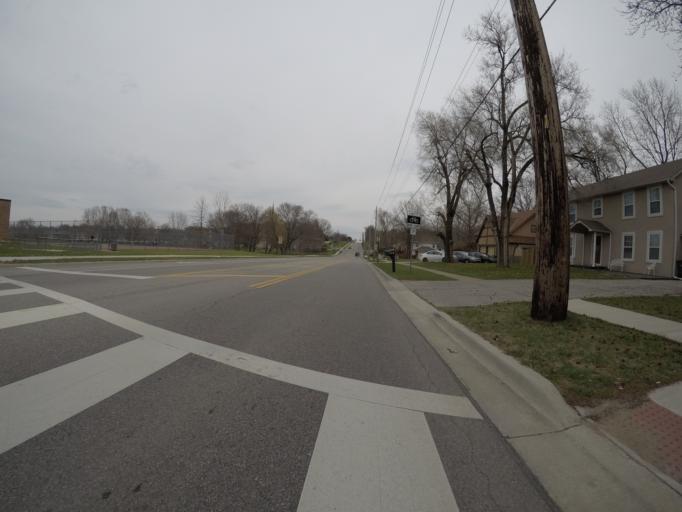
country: US
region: Kansas
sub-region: Johnson County
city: Olathe
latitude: 38.8691
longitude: -94.7878
